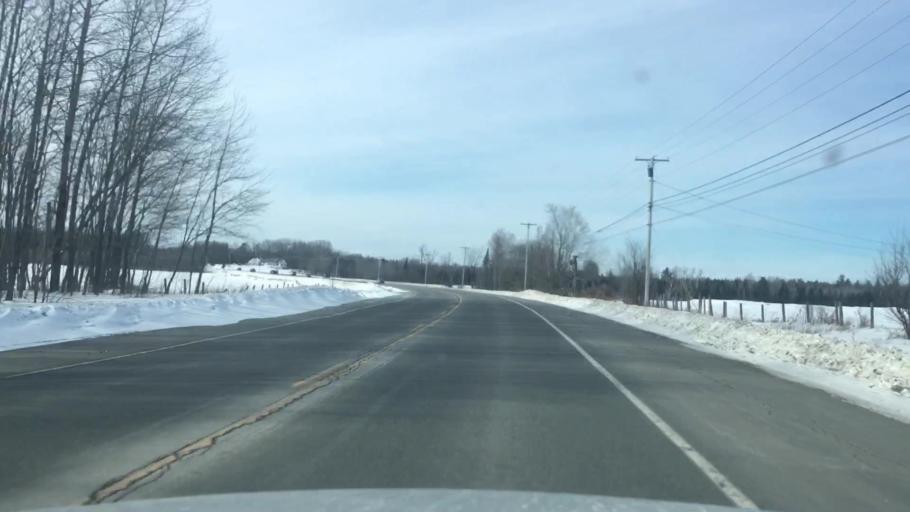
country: US
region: Maine
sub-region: Penobscot County
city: Kenduskeag
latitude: 44.9092
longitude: -68.8962
